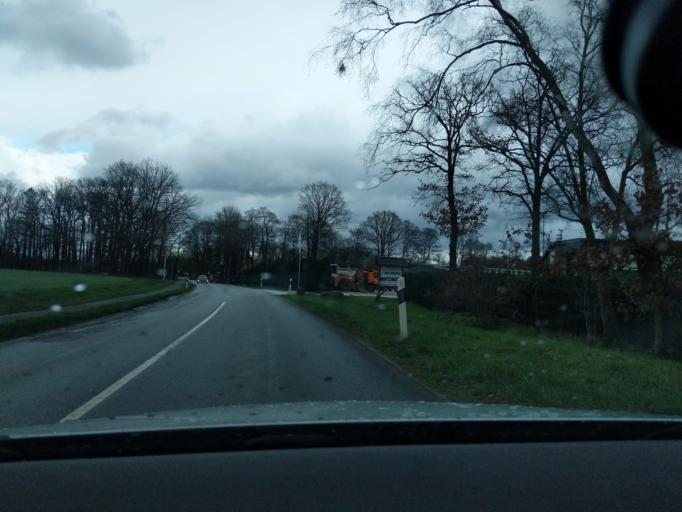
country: DE
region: Lower Saxony
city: Kutenholz
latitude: 53.5165
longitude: 9.3768
